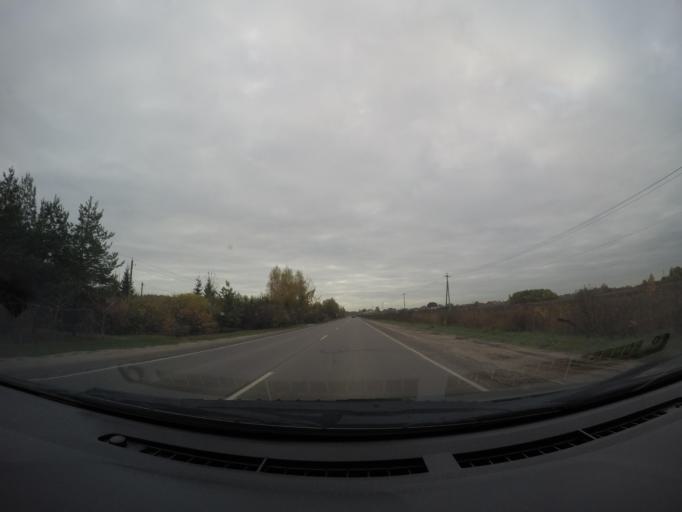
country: RU
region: Moskovskaya
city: Staraya Kupavna
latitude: 55.7700
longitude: 38.2010
